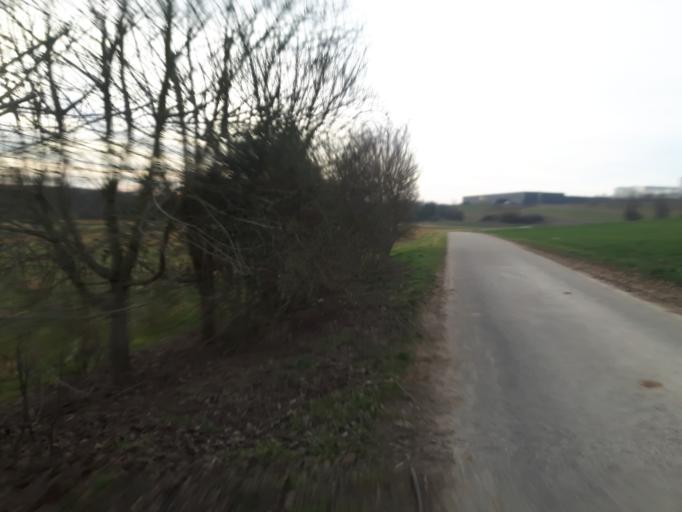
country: DE
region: Baden-Wuerttemberg
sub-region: Regierungsbezirk Stuttgart
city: Neuenstadt am Kocher
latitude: 49.2280
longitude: 9.3610
